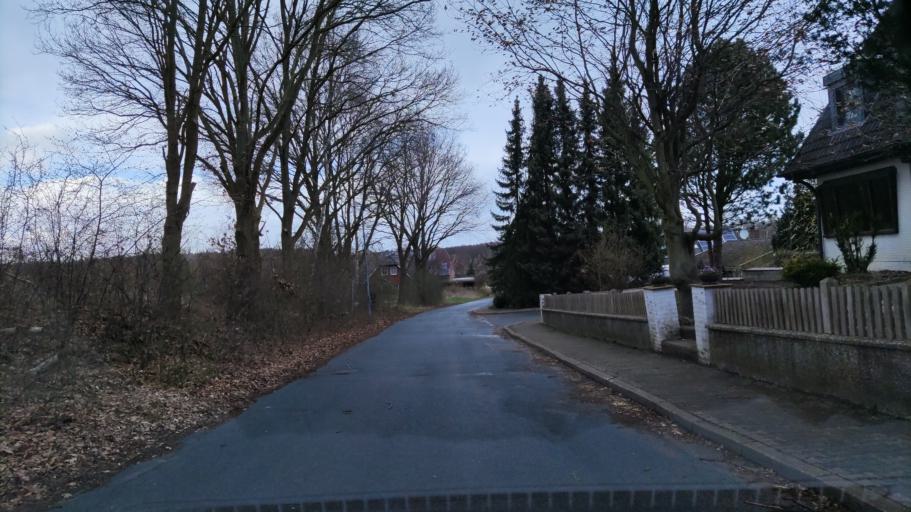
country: DE
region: Lower Saxony
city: Dahlenburg
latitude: 53.1921
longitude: 10.7264
